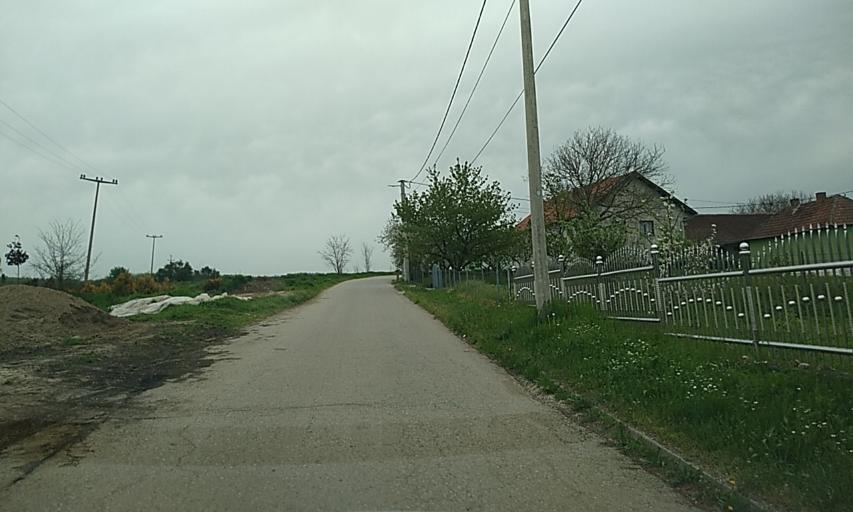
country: RS
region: Central Serbia
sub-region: Nisavski Okrug
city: Razanj
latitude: 43.5730
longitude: 21.5042
